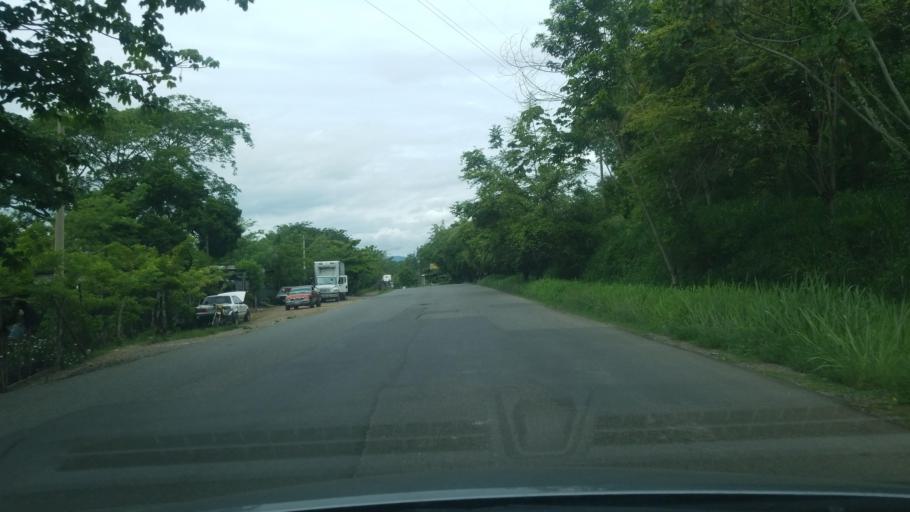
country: HN
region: Santa Barbara
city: La Flecha
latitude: 15.2994
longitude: -88.4812
